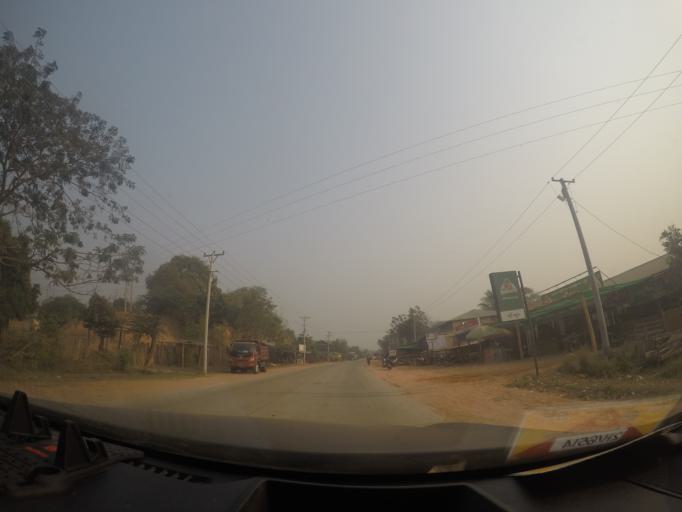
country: MM
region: Mandalay
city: Nay Pyi Taw
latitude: 19.9129
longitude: 96.0237
